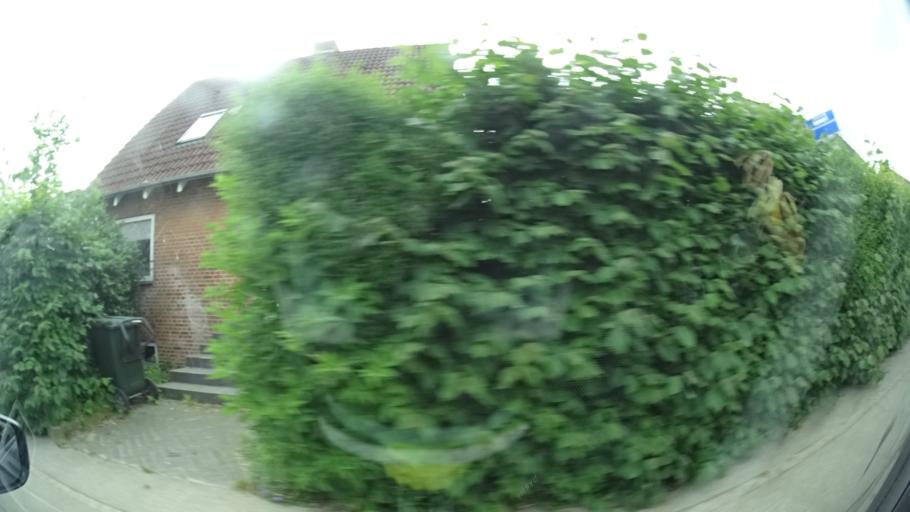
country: DK
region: Central Jutland
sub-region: Syddjurs Kommune
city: Ryomgard
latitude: 56.3821
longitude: 10.5068
